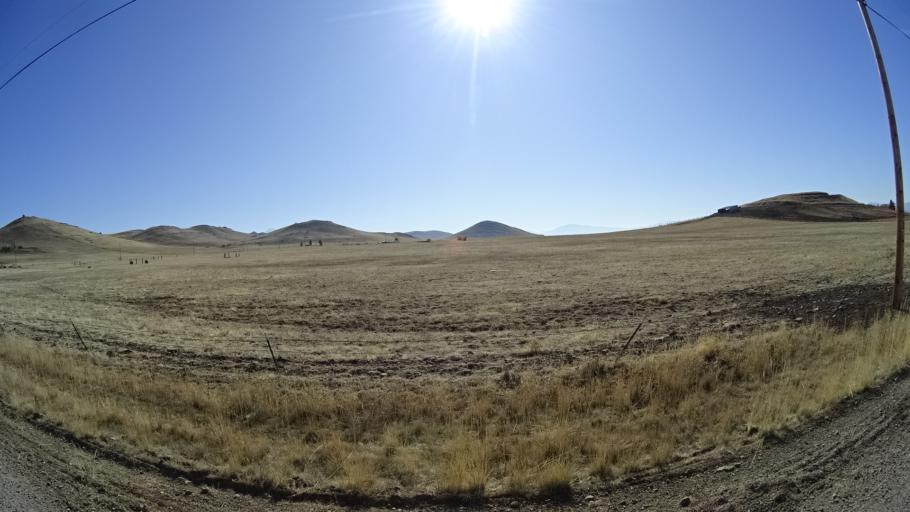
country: US
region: California
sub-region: Siskiyou County
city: Montague
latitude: 41.7939
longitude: -122.4273
